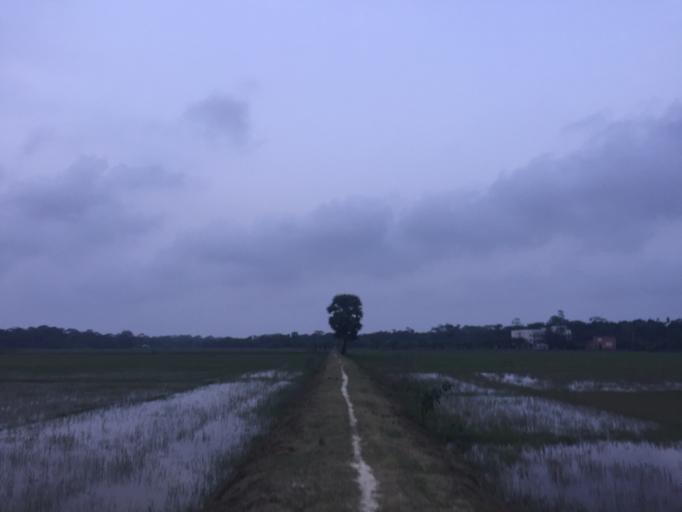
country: BD
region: Barisal
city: Mathba
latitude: 22.1913
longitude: 89.9344
